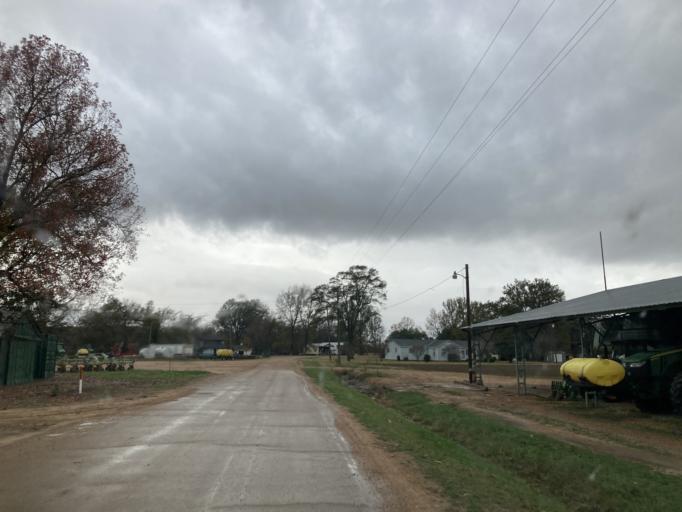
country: US
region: Mississippi
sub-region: Yazoo County
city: Yazoo City
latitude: 32.9877
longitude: -90.4456
